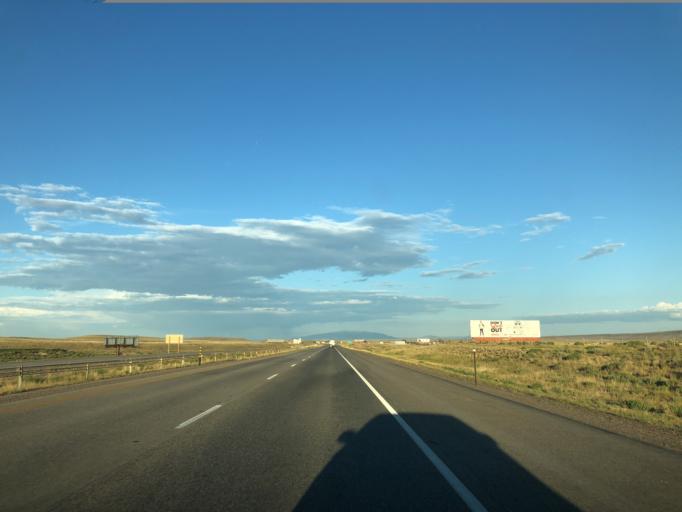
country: US
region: Wyoming
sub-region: Carbon County
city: Rawlins
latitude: 41.7869
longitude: -107.1851
